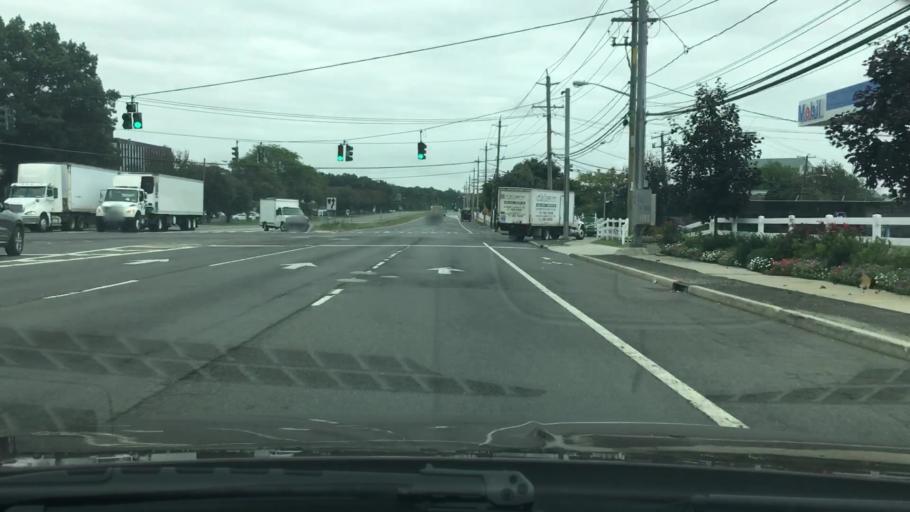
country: US
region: New York
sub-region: Suffolk County
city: Islandia
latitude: 40.8066
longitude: -73.1822
